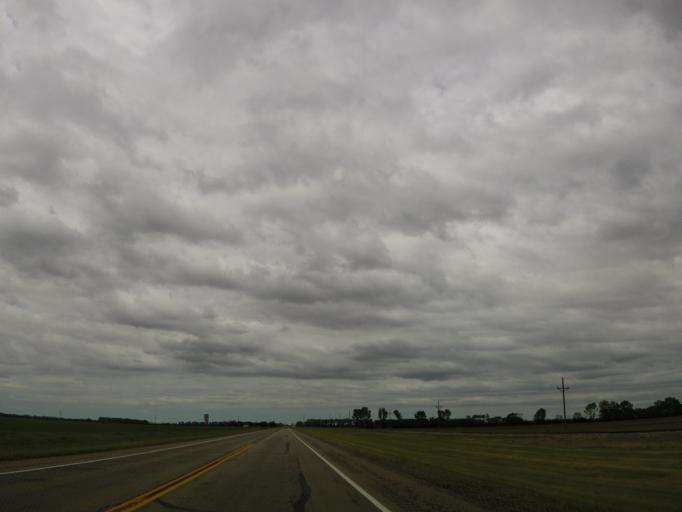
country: US
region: North Dakota
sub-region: Walsh County
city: Grafton
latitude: 48.5747
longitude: -97.4478
